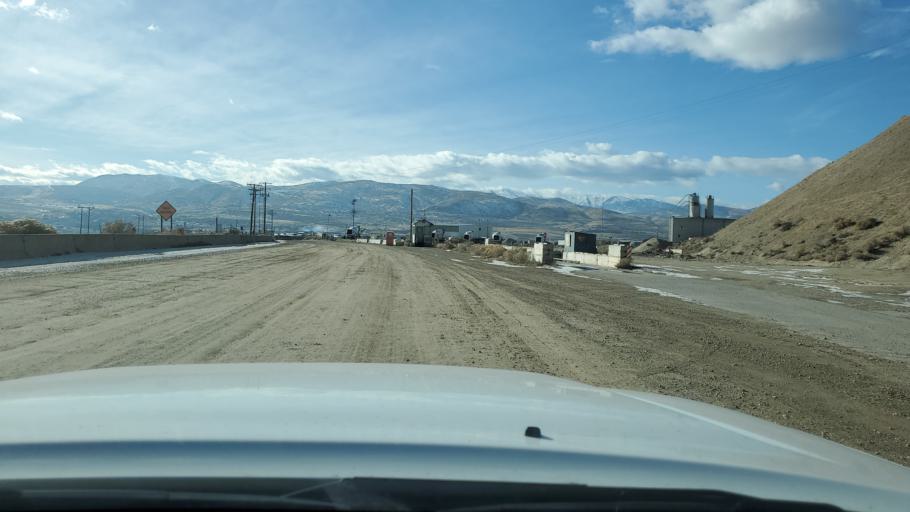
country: US
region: Utah
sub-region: Salt Lake County
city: Bluffdale
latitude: 40.4514
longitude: -111.9077
